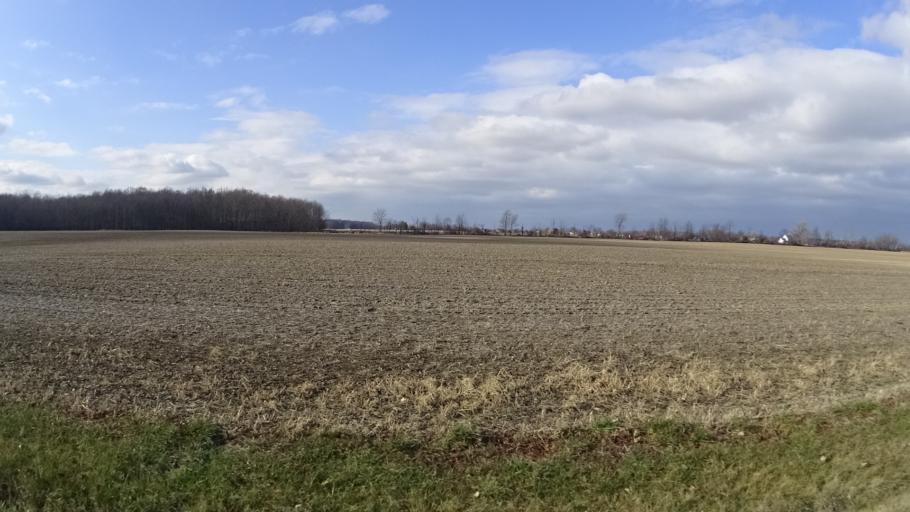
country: US
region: Ohio
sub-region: Lorain County
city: Camden
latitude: 41.2337
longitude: -82.2897
